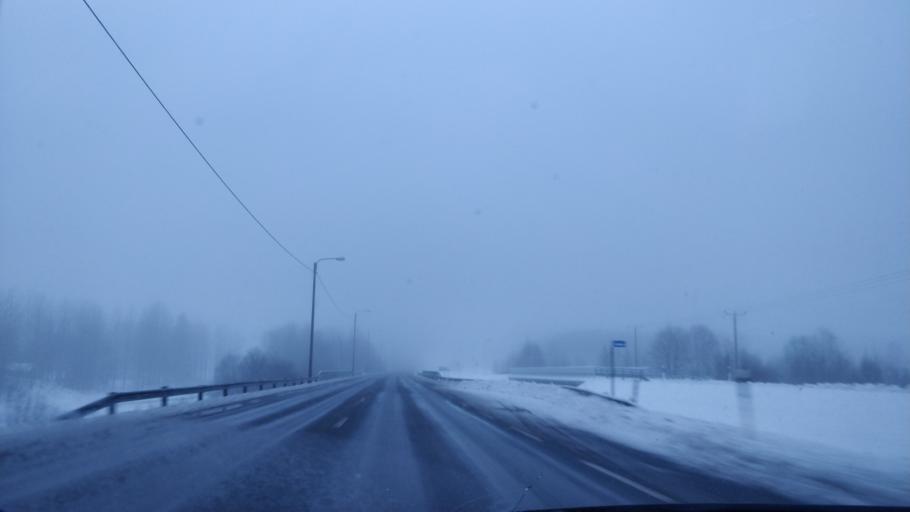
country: FI
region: Lapland
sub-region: Kemi-Tornio
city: Tervola
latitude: 66.1402
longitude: 24.9435
